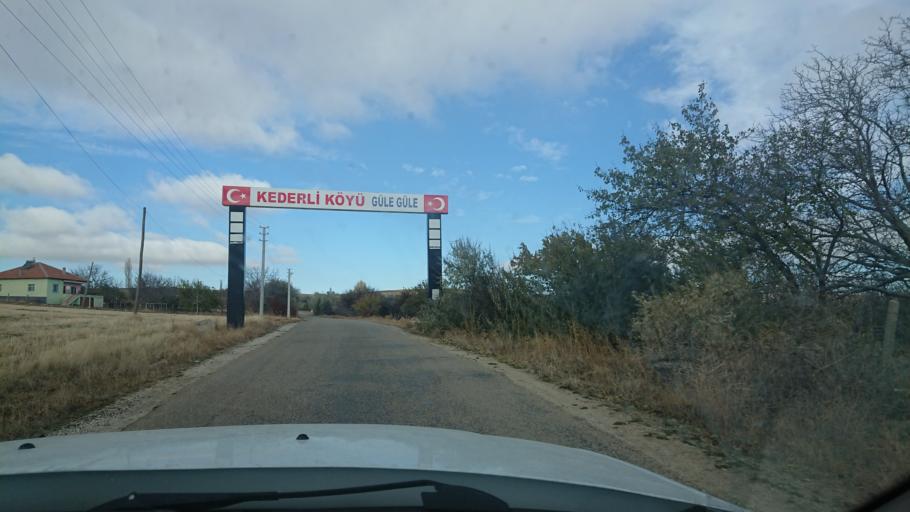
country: TR
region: Aksaray
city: Agacoren
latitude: 38.8272
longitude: 33.9578
